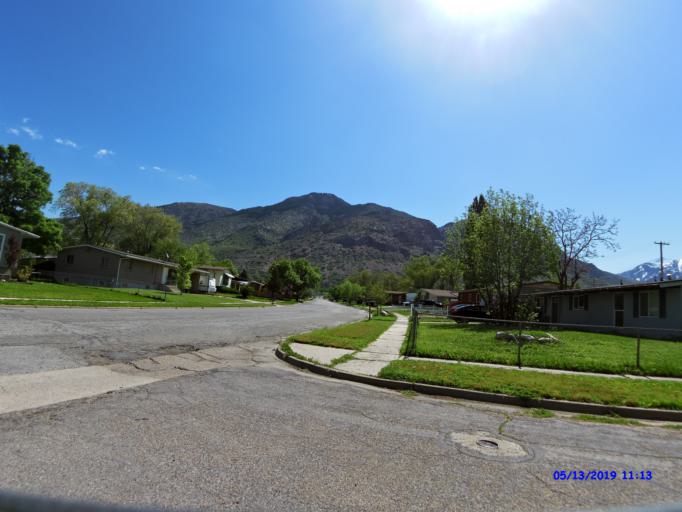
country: US
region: Utah
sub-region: Weber County
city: Harrisville
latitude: 41.2799
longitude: -111.9628
